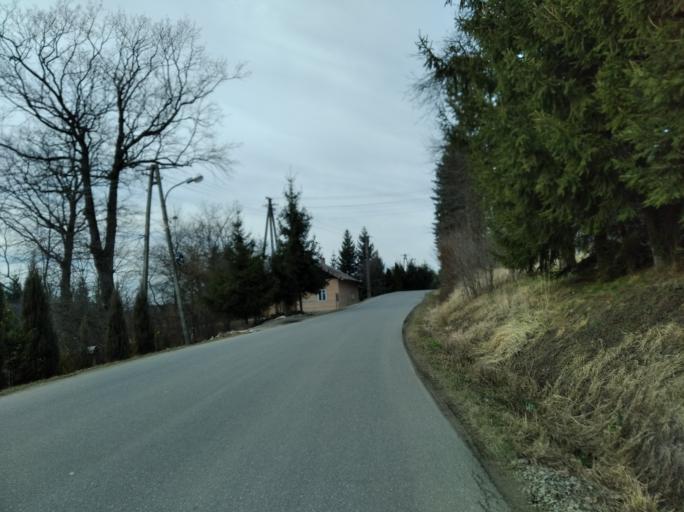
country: PL
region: Subcarpathian Voivodeship
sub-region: Powiat brzozowski
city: Gorki
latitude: 49.6487
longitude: 22.0364
